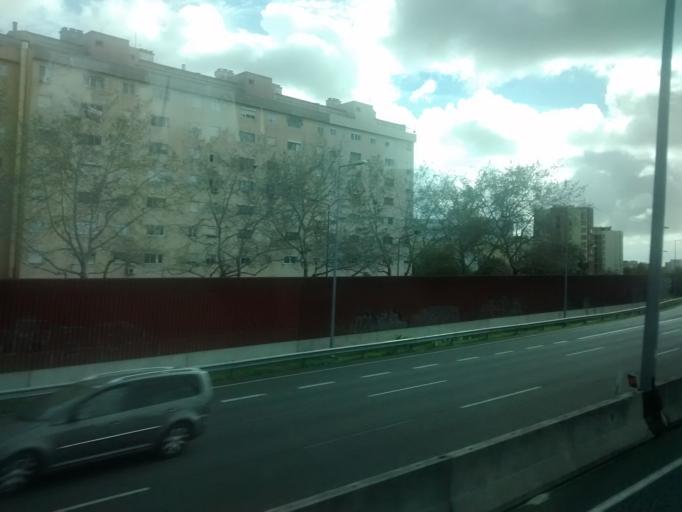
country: PT
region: Lisbon
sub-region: Odivelas
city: Olival do Basto
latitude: 38.7657
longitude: -9.1728
